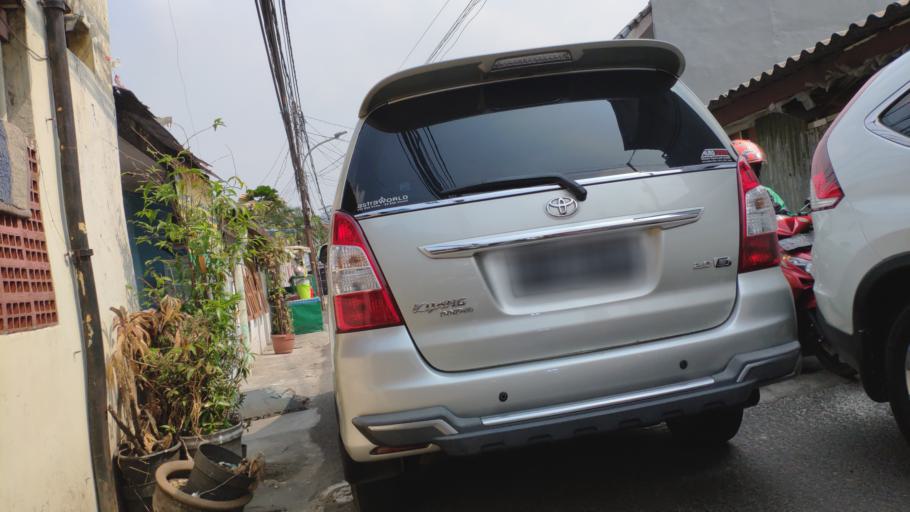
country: ID
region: Banten
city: South Tangerang
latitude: -6.2873
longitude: 106.7904
